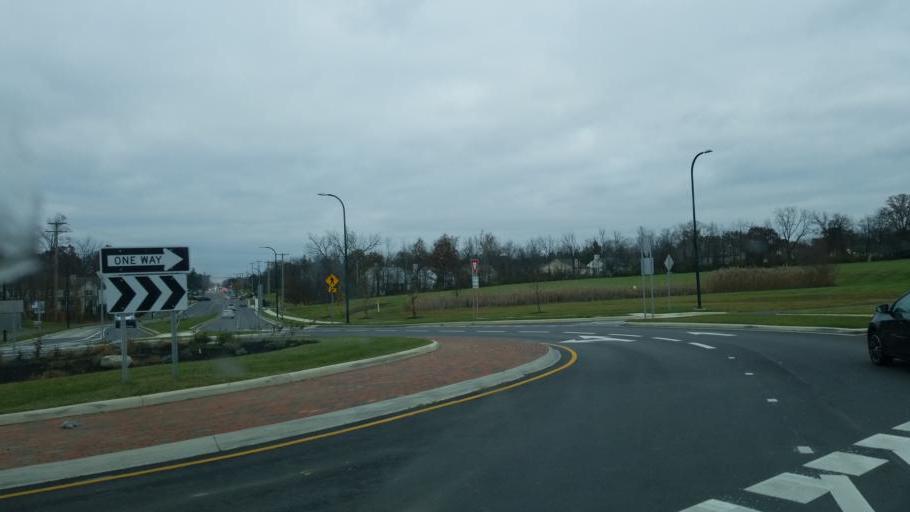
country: US
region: Ohio
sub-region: Franklin County
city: Gahanna
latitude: 40.0316
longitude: -82.8655
